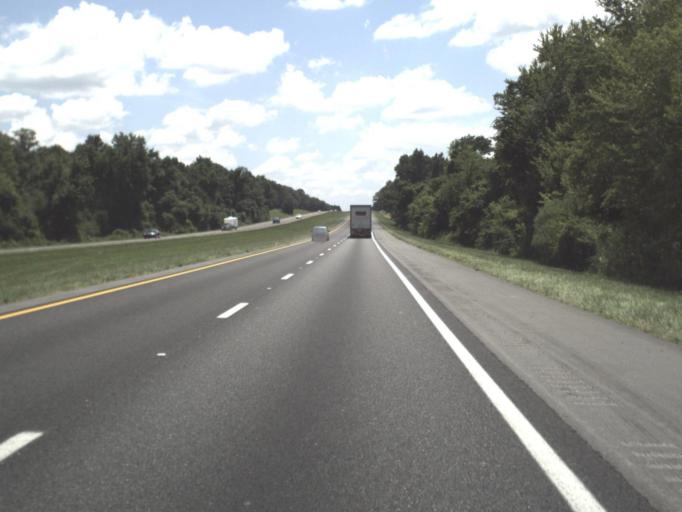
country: US
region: Florida
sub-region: Madison County
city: Madison
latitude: 30.4362
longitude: -83.5119
